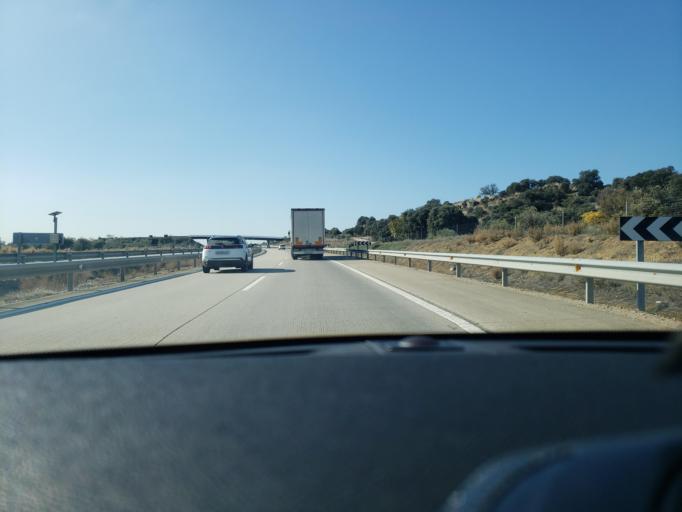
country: ES
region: Castille-La Mancha
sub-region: Province of Toledo
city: Cervera de los Montes
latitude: 40.0193
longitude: -4.8017
